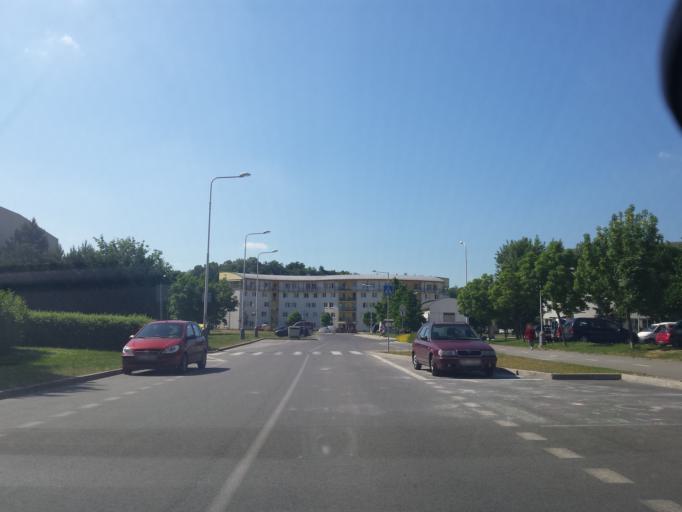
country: CZ
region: Central Bohemia
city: Kralupy nad Vltavou
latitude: 50.2440
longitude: 14.3080
